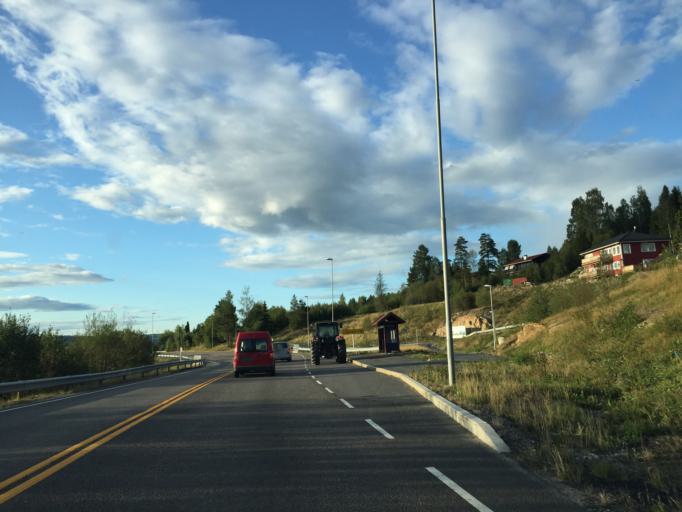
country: NO
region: Akershus
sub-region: Fet
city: Fetsund
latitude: 59.9171
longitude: 11.1841
